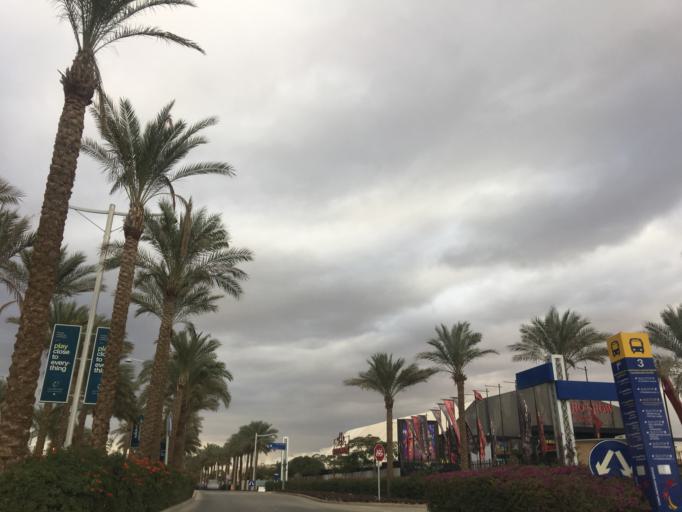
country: EG
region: Muhafazat al Qahirah
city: Cairo
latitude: 30.0296
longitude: 31.4108
